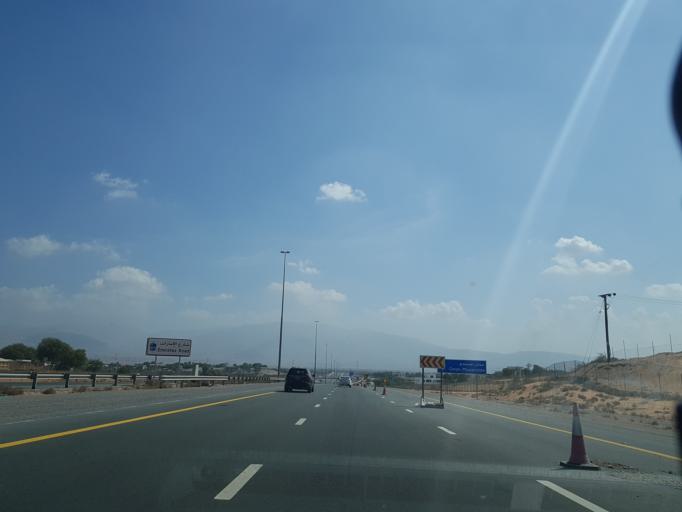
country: AE
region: Ra's al Khaymah
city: Ras al-Khaimah
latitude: 25.7039
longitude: 55.9538
